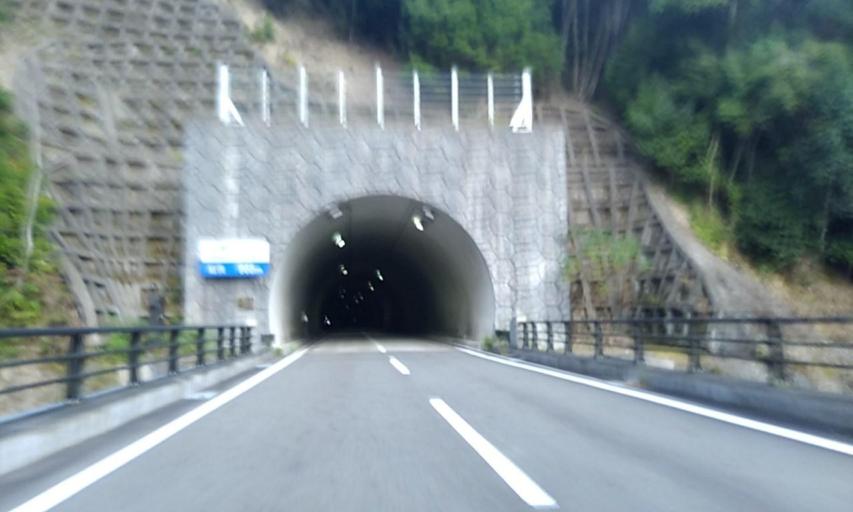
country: JP
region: Wakayama
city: Shingu
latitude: 33.8804
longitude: 135.8771
